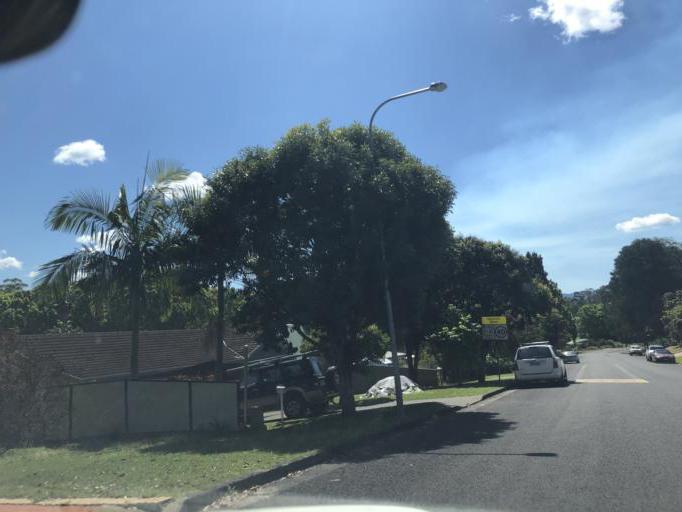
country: AU
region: New South Wales
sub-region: Bellingen
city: Bellingen
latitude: -30.4581
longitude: 152.9060
